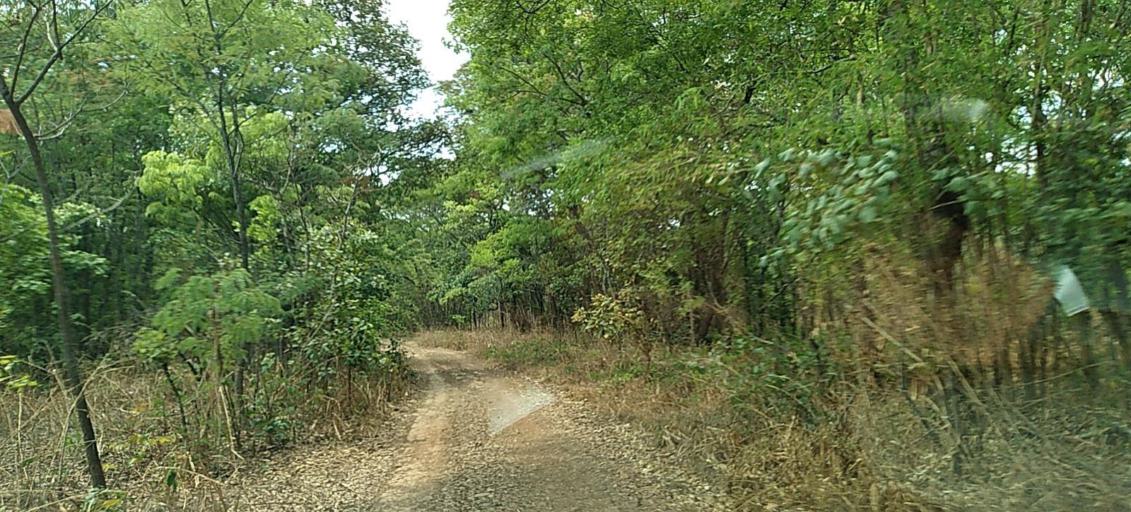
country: ZM
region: Copperbelt
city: Chililabombwe
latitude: -12.4726
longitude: 27.6513
